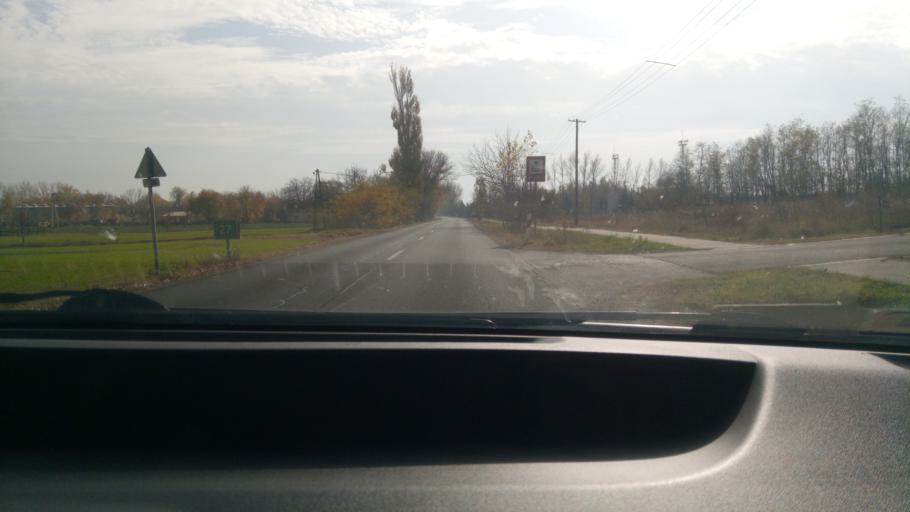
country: HU
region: Bacs-Kiskun
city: Kiskunmajsa
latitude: 46.5265
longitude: 19.7438
